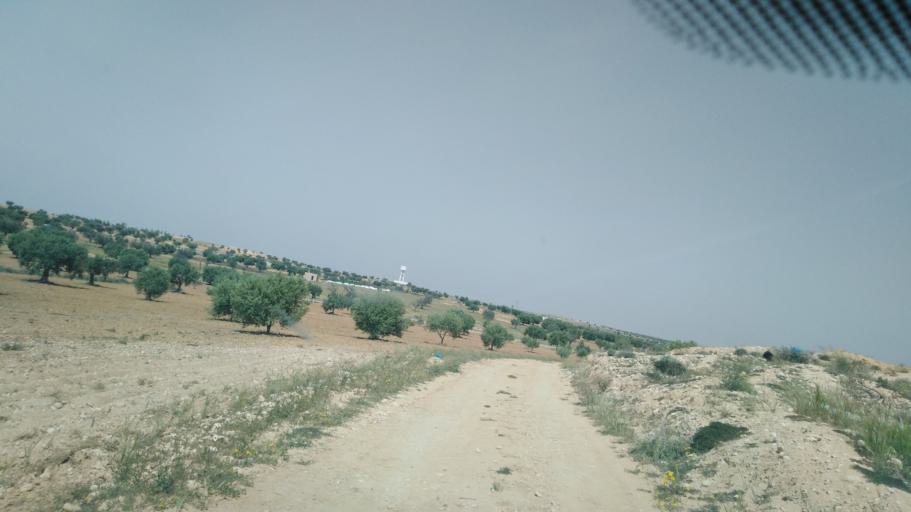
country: TN
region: Safaqis
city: Sfax
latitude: 34.7479
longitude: 10.5675
